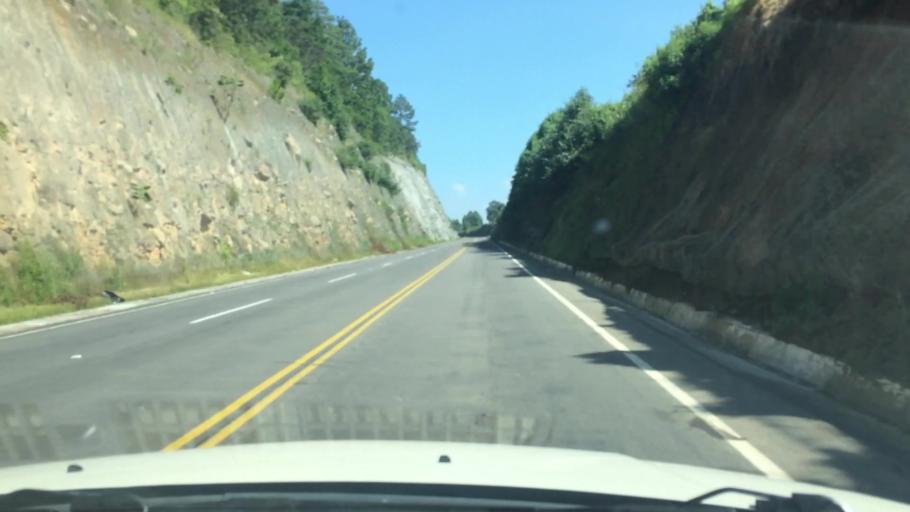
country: MX
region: Mexico
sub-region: Amanalco
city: San Bartolo
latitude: 19.2402
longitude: -100.0664
